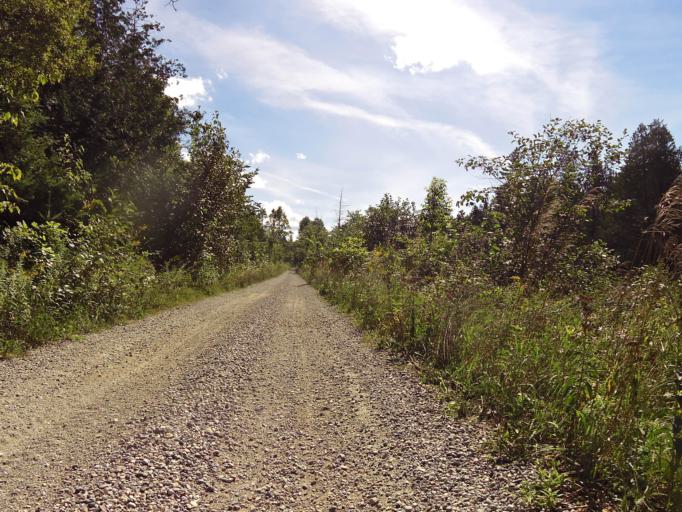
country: CA
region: Ontario
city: Renfrew
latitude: 45.0382
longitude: -76.7033
